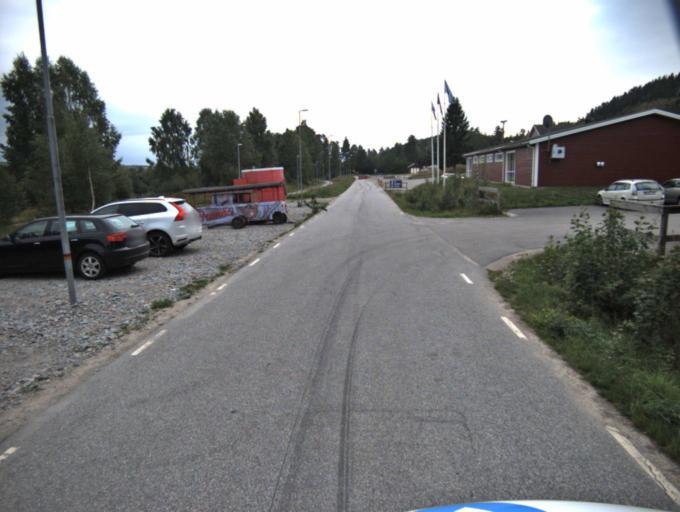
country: SE
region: Vaestra Goetaland
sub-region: Ulricehamns Kommun
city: Ulricehamn
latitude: 57.8206
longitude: 13.4135
